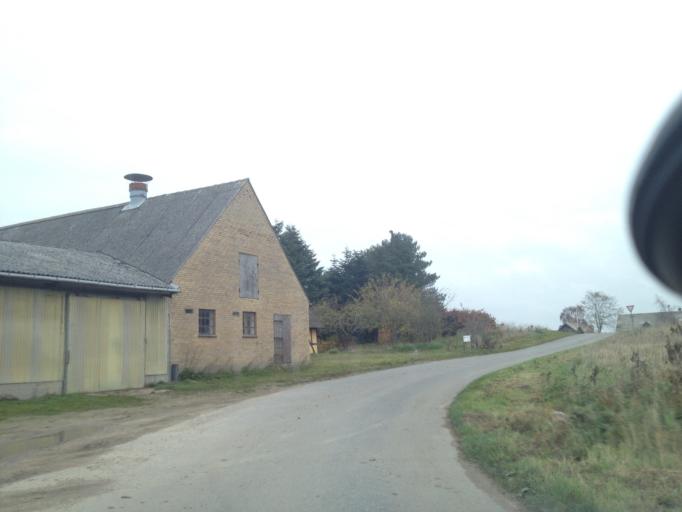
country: DK
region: South Denmark
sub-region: Nordfyns Kommune
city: Sonderso
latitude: 55.4256
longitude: 10.2170
